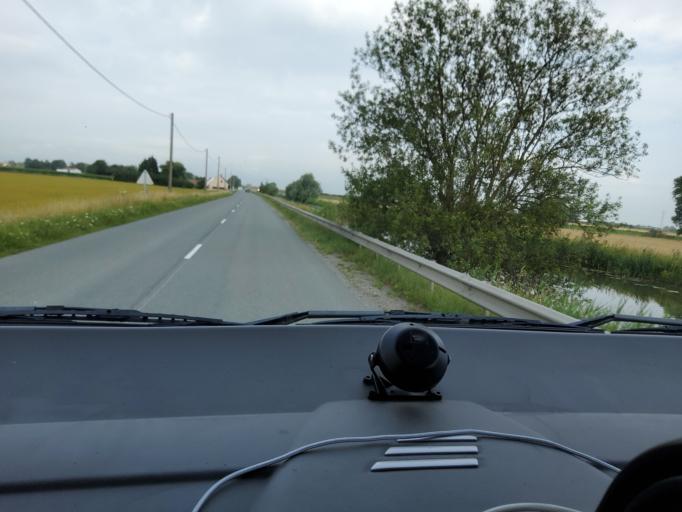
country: FR
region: Nord-Pas-de-Calais
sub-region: Departement du Nord
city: Bourbourg
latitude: 50.9518
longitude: 2.2354
